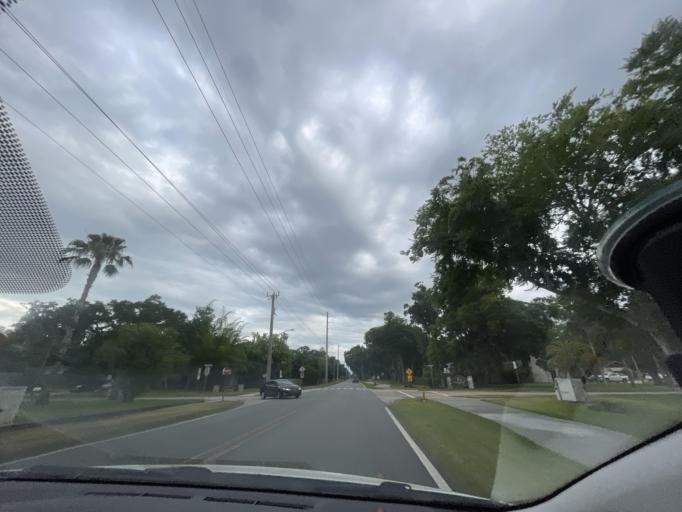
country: US
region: Florida
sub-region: Volusia County
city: Port Orange
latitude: 29.0979
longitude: -80.9931
